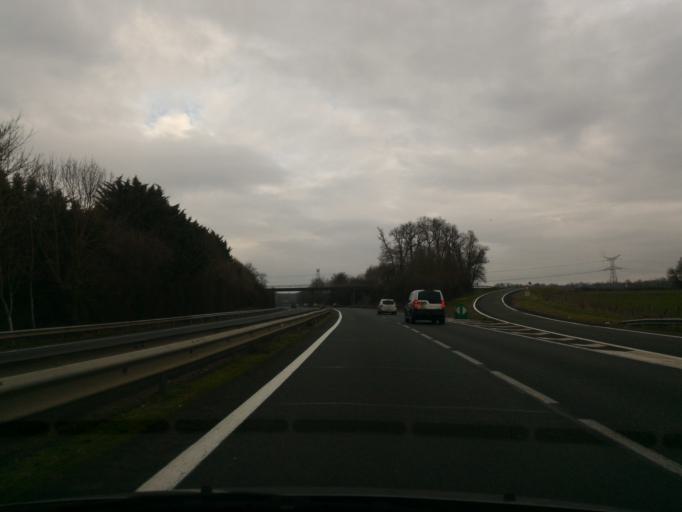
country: FR
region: Poitou-Charentes
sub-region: Departement de la Vienne
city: Celle-Levescault
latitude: 46.3676
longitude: 0.2078
